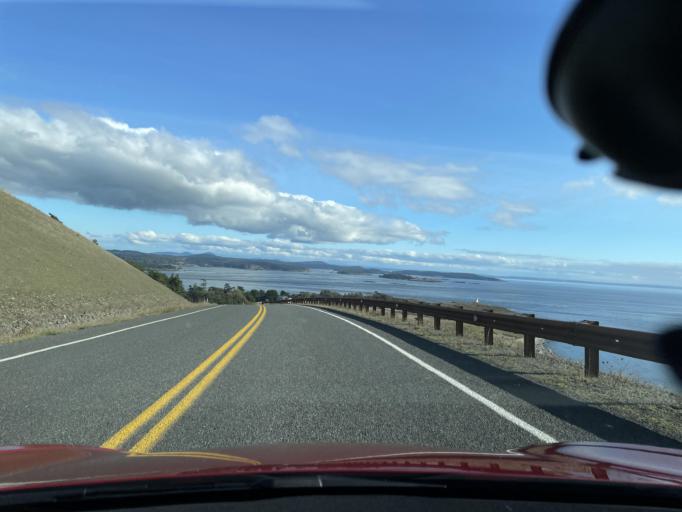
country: US
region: Washington
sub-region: San Juan County
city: Friday Harbor
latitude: 48.4550
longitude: -122.9752
